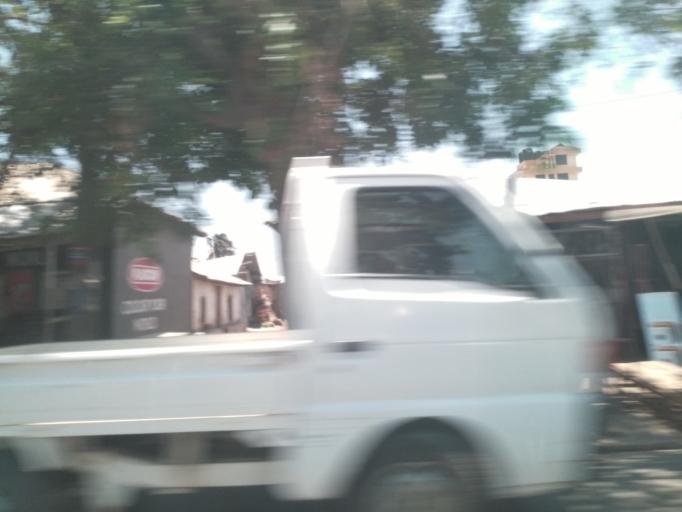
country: TZ
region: Dodoma
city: Dodoma
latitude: -6.1739
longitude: 35.7447
